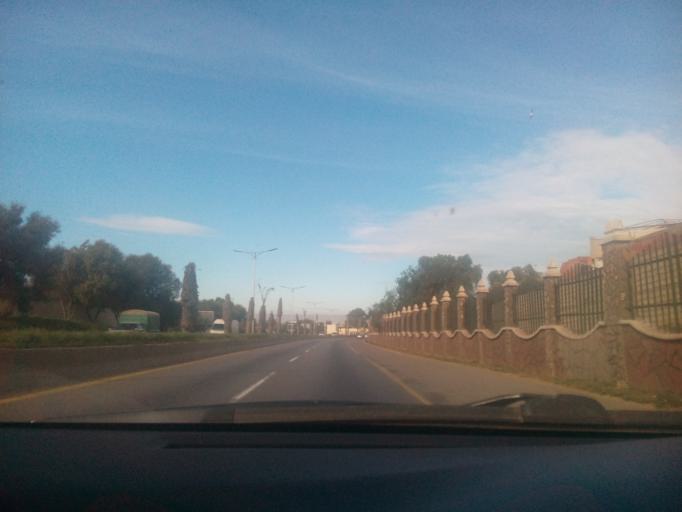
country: DZ
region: Oran
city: Es Senia
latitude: 35.6122
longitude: -0.5811
